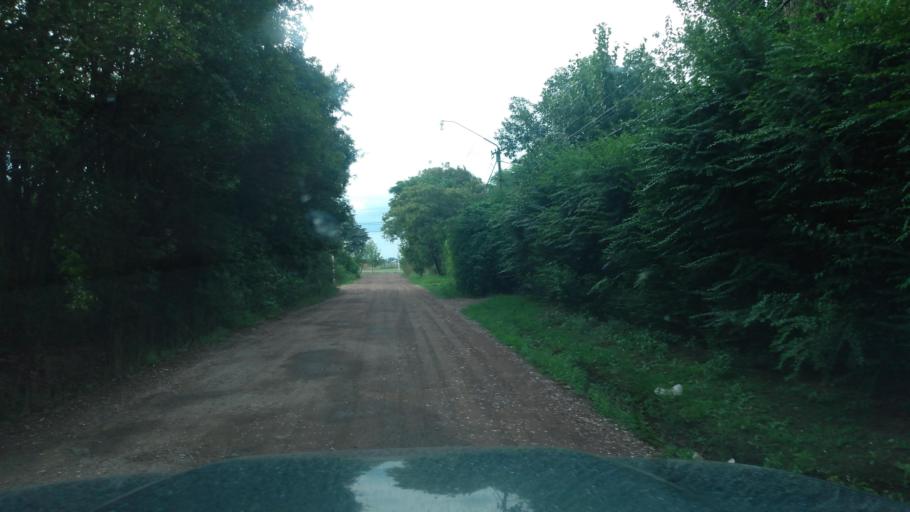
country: AR
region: Buenos Aires
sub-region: Partido de Lujan
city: Lujan
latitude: -34.5462
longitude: -59.1265
